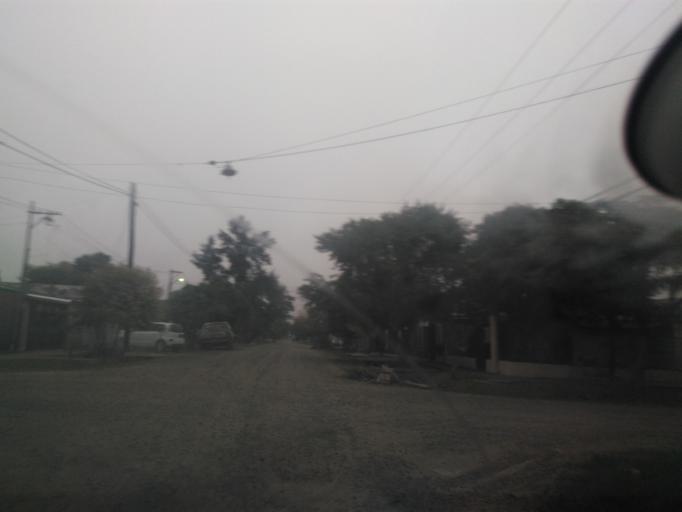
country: AR
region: Chaco
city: Resistencia
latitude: -27.4693
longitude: -58.9964
